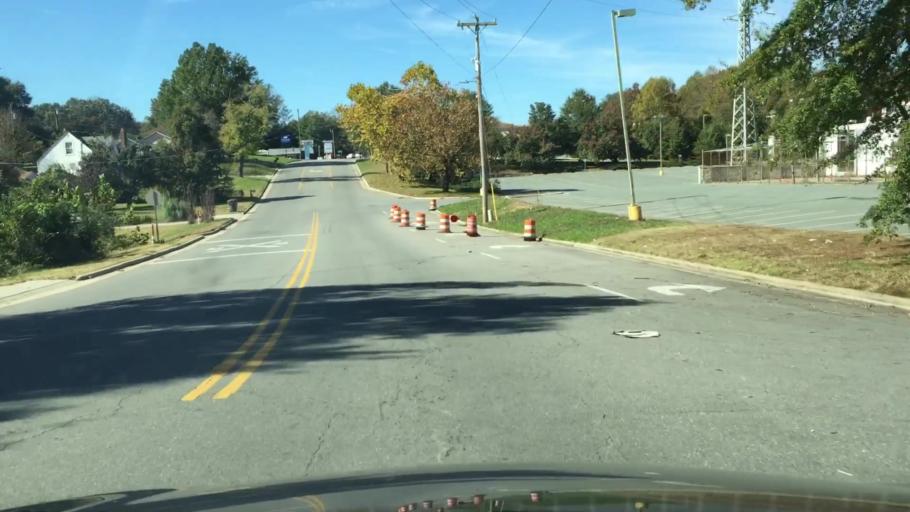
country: US
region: North Carolina
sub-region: Rockingham County
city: Reidsville
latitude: 36.3391
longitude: -79.6566
